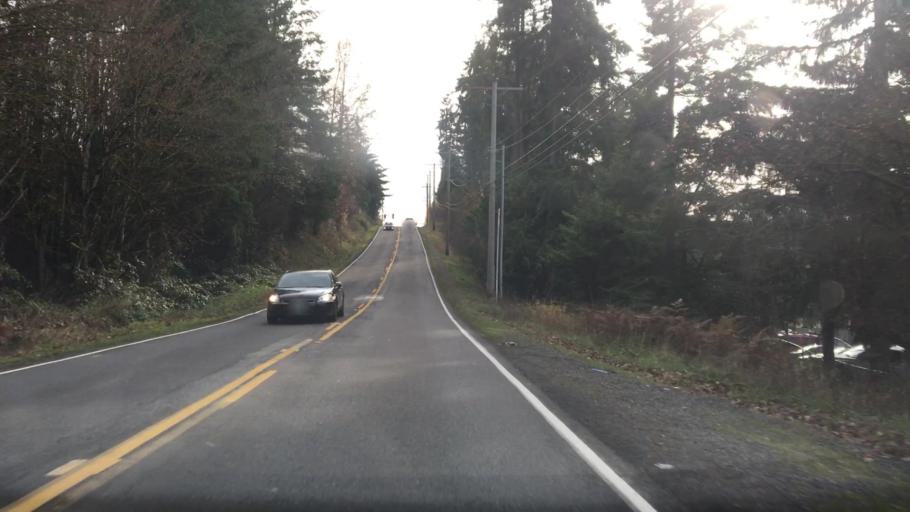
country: US
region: Washington
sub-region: Pierce County
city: Frederickson
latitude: 47.1138
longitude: -122.3255
